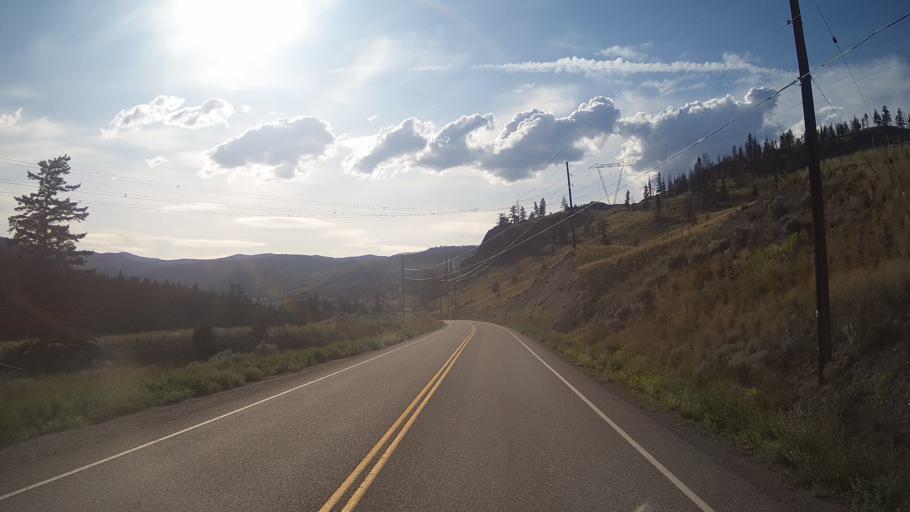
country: CA
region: British Columbia
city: Cache Creek
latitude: 50.8851
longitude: -121.4310
